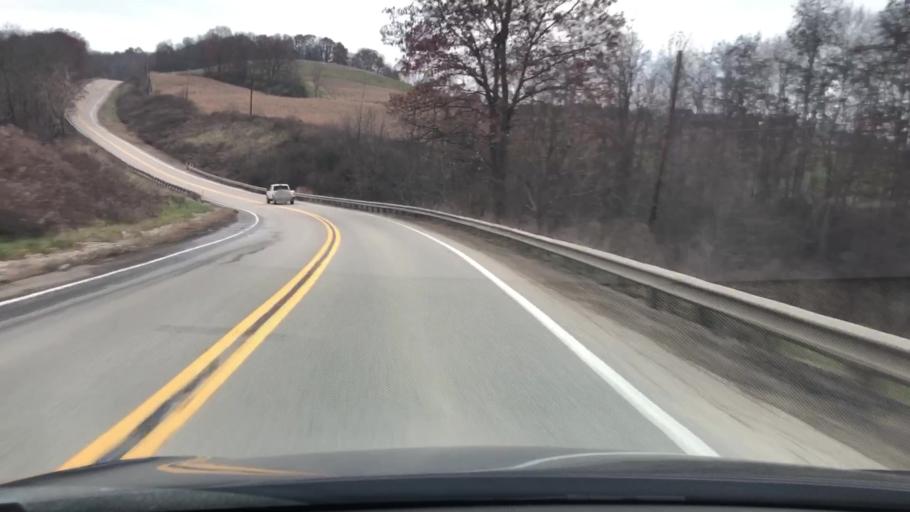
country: US
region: Pennsylvania
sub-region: Armstrong County
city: Kittanning
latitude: 40.8348
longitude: -79.4711
